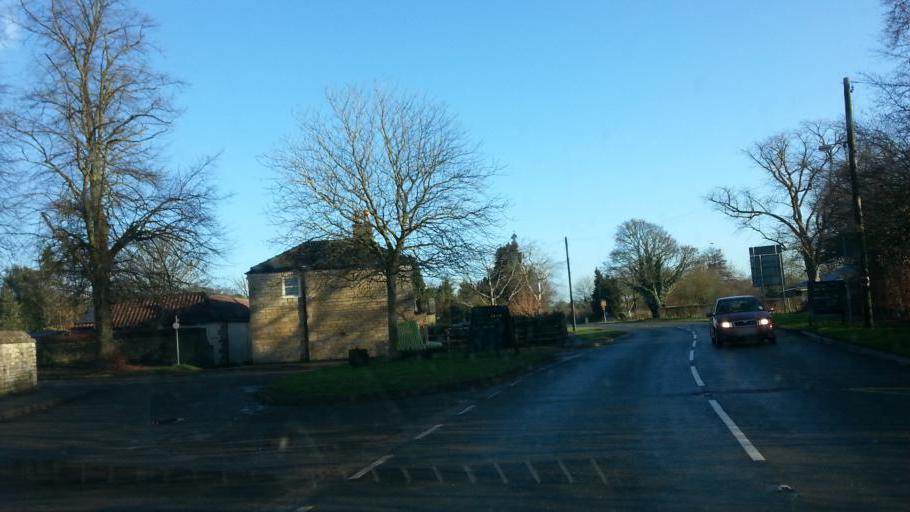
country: GB
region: England
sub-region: Lincolnshire
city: Navenby
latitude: 53.0578
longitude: -0.5822
